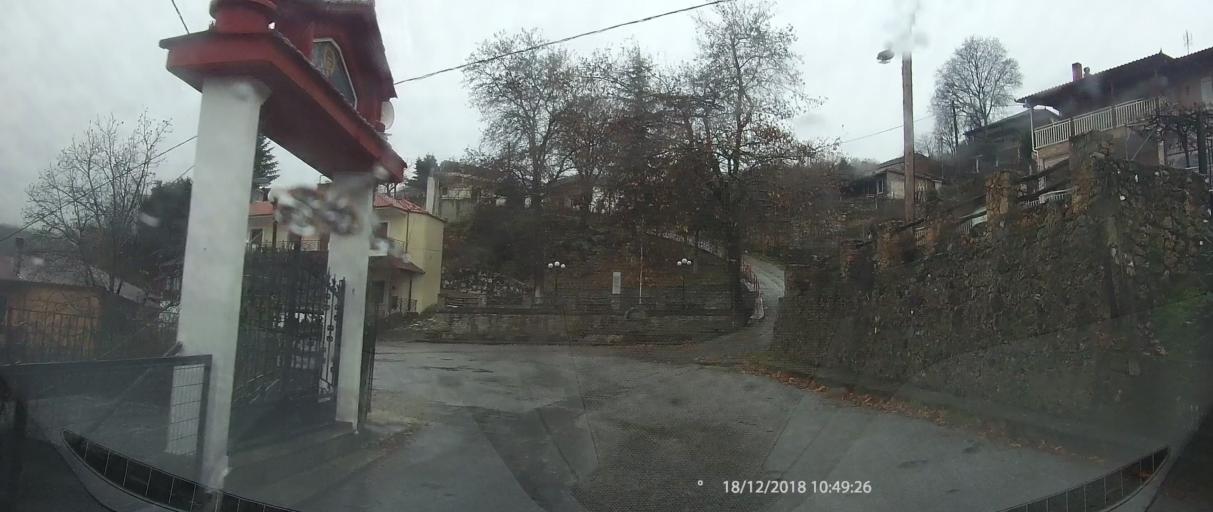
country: GR
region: Central Macedonia
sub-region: Nomos Pierias
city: Kato Milia
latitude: 40.1805
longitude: 22.3306
